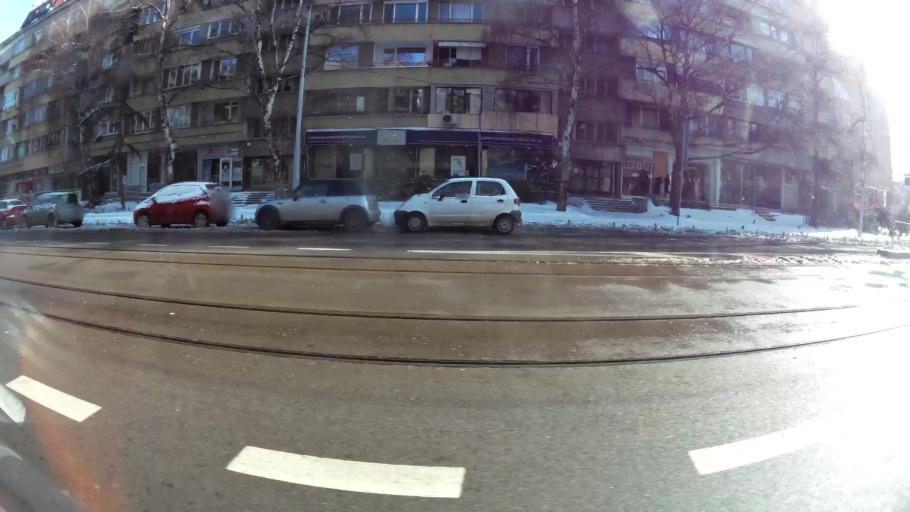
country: BG
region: Sofia-Capital
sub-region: Stolichna Obshtina
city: Sofia
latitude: 42.6798
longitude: 23.3113
